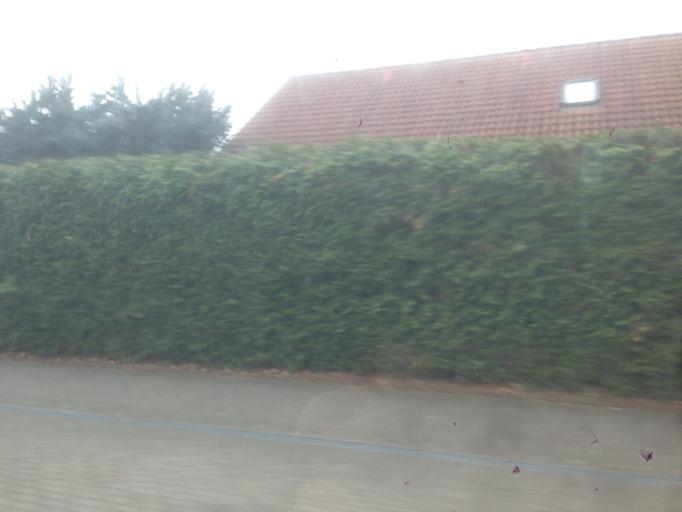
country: DE
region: Berlin
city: Blankenfelde
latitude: 52.6460
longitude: 13.3765
